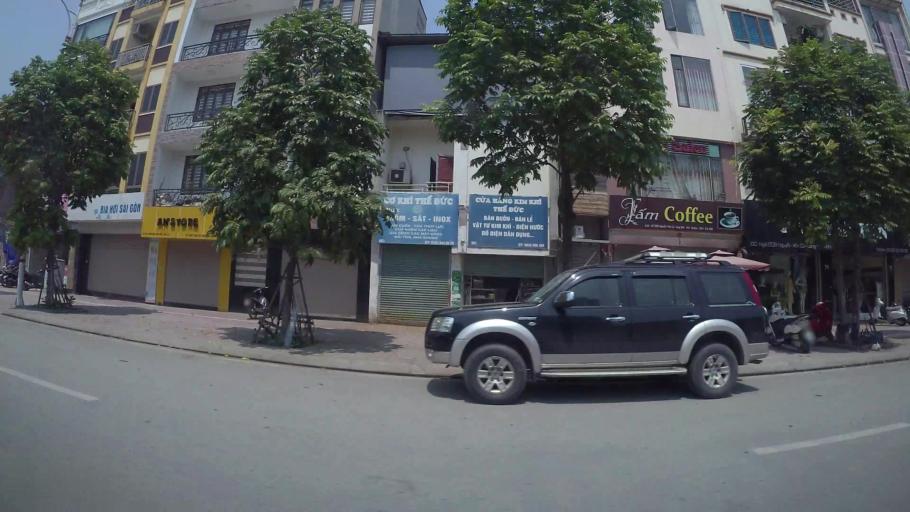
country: VN
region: Ha Noi
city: Hoan Kiem
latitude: 21.0422
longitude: 105.8737
